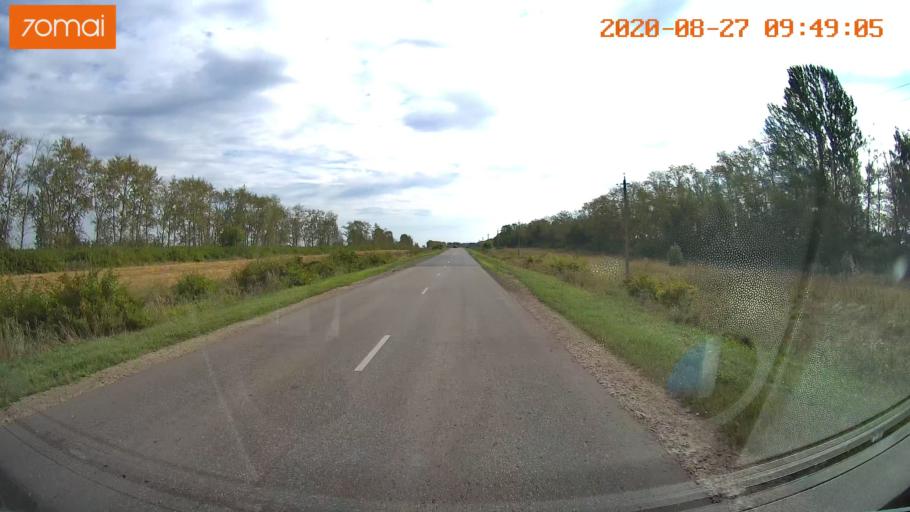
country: RU
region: Tula
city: Kurkino
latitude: 53.4086
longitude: 38.5815
